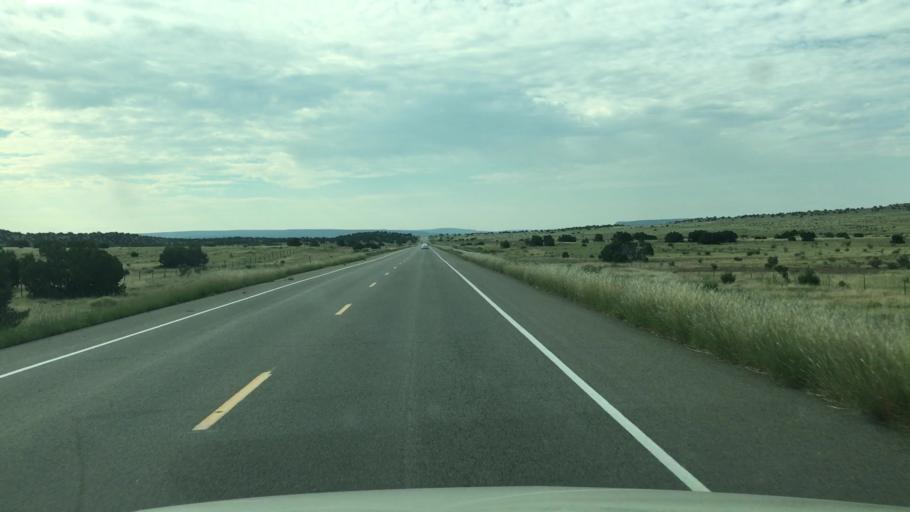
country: US
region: New Mexico
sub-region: Santa Fe County
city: Eldorado at Santa Fe
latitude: 35.4438
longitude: -105.8867
